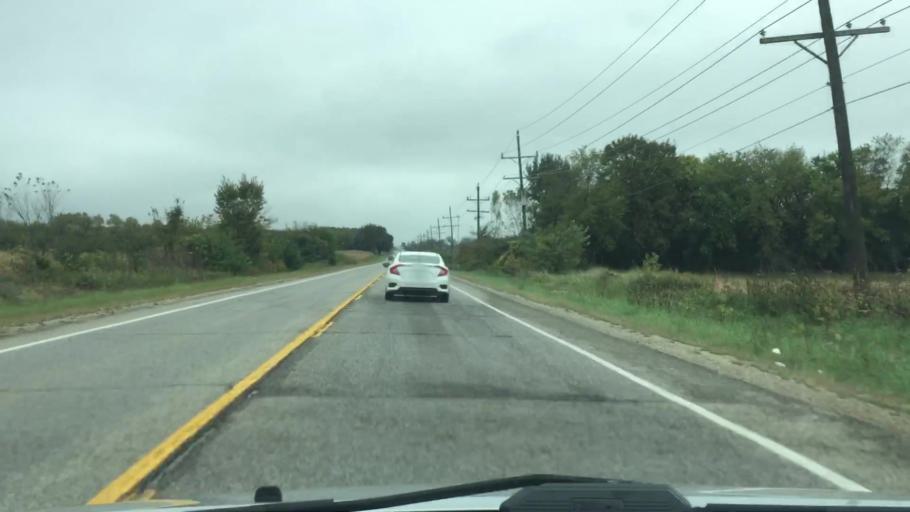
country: US
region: Illinois
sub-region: McHenry County
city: Prairie Grove
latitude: 42.2965
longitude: -88.2871
